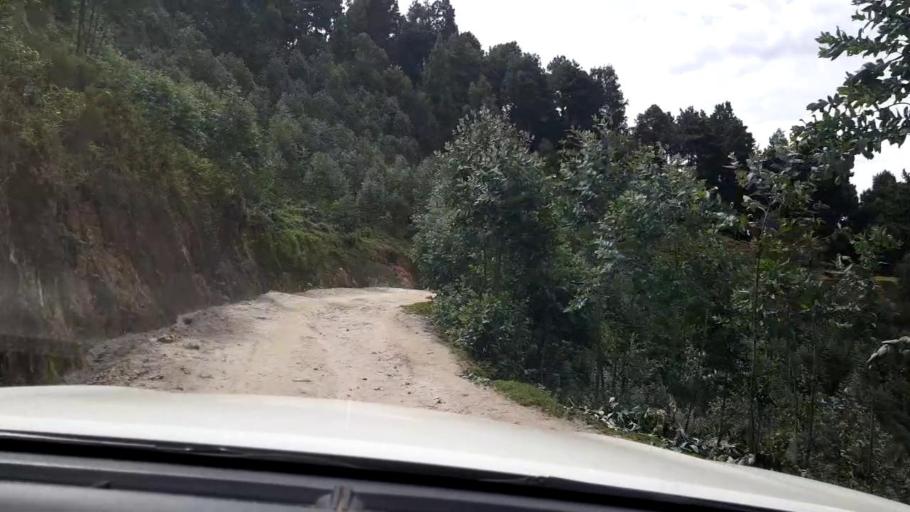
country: RW
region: Western Province
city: Kibuye
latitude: -1.8754
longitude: 29.4531
